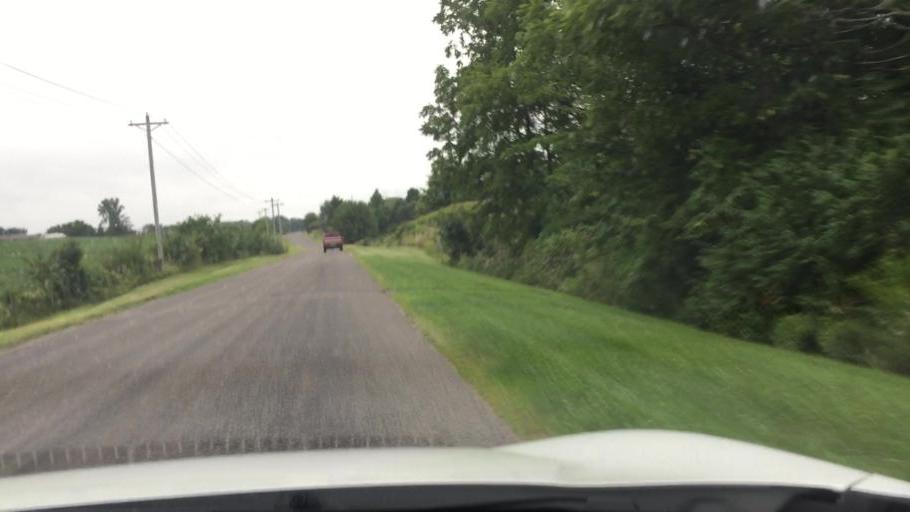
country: US
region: Ohio
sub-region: Champaign County
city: Mechanicsburg
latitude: 40.0445
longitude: -83.5851
